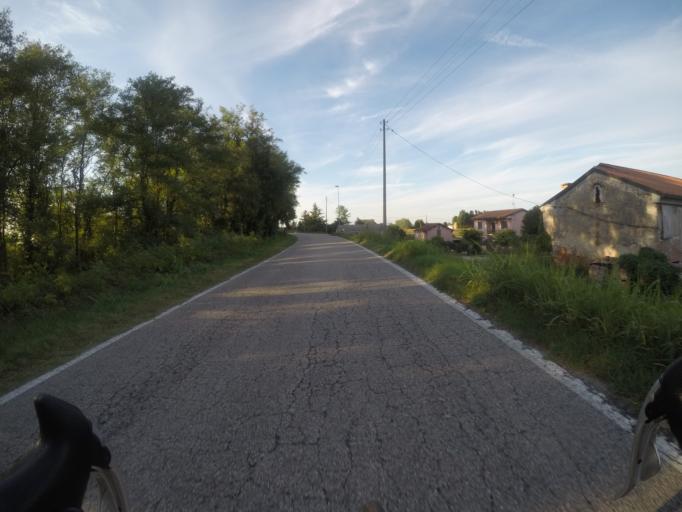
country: IT
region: Veneto
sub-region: Provincia di Rovigo
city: San Bellino
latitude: 45.0139
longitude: 11.5658
